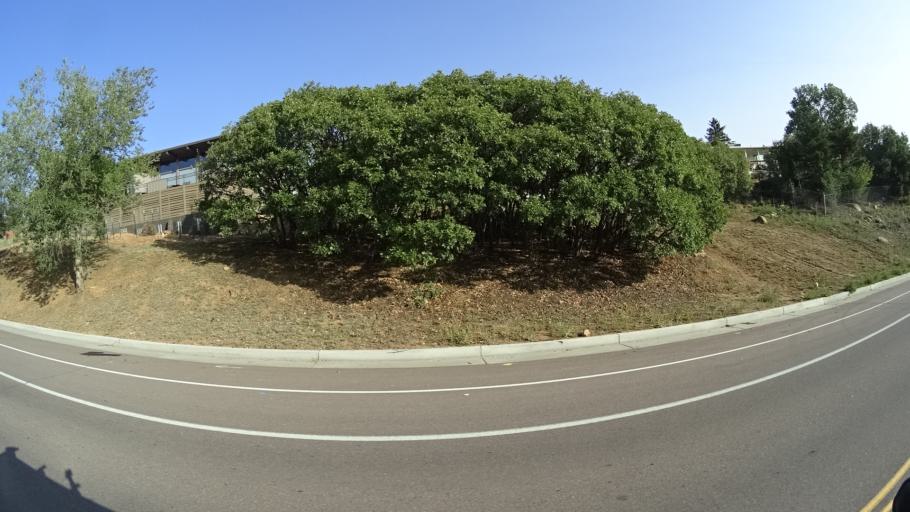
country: US
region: Colorado
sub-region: El Paso County
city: Colorado Springs
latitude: 38.8132
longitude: -104.8564
